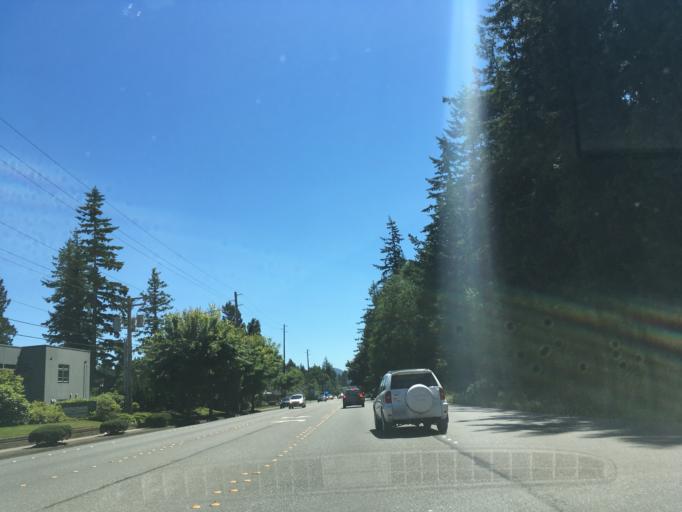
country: US
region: Washington
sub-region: Whatcom County
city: Bellingham
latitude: 48.7809
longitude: -122.4863
